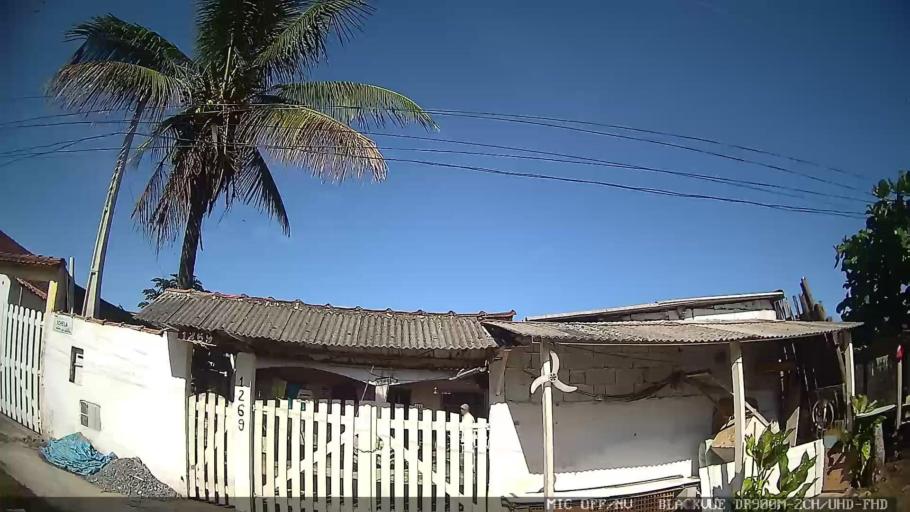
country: BR
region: Sao Paulo
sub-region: Itanhaem
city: Itanhaem
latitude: -24.2248
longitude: -46.8793
